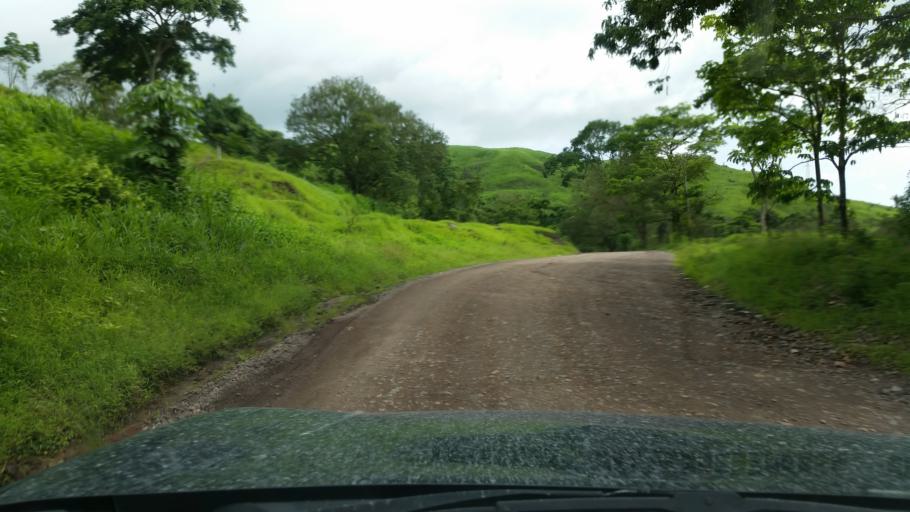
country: NI
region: Atlantico Norte (RAAN)
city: Siuna
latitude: 13.5250
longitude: -84.8232
